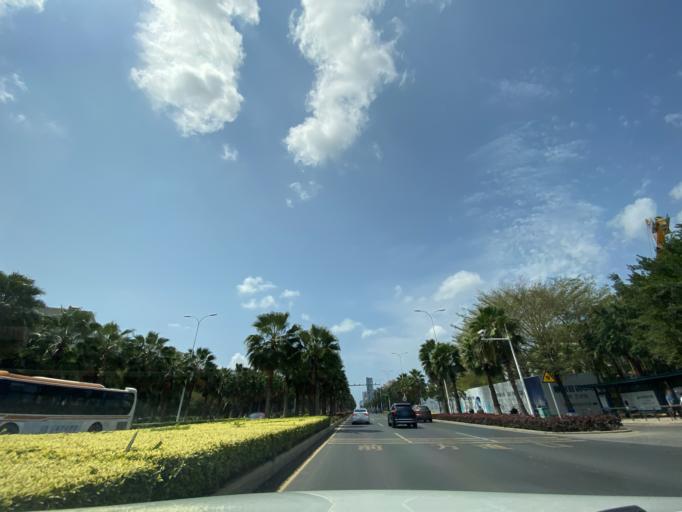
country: CN
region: Hainan
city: Sanya
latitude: 18.2853
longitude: 109.5186
